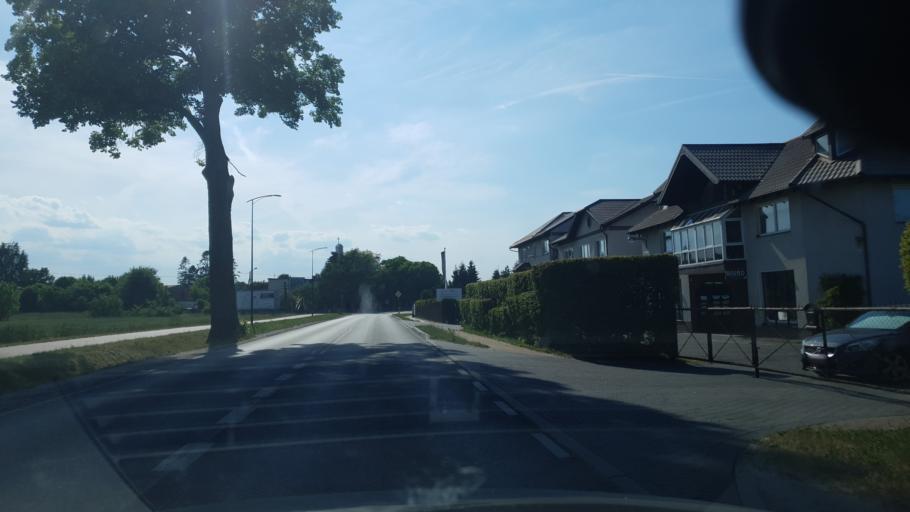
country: PL
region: Pomeranian Voivodeship
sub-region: Powiat kartuski
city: Chwaszczyno
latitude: 54.4427
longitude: 18.4259
